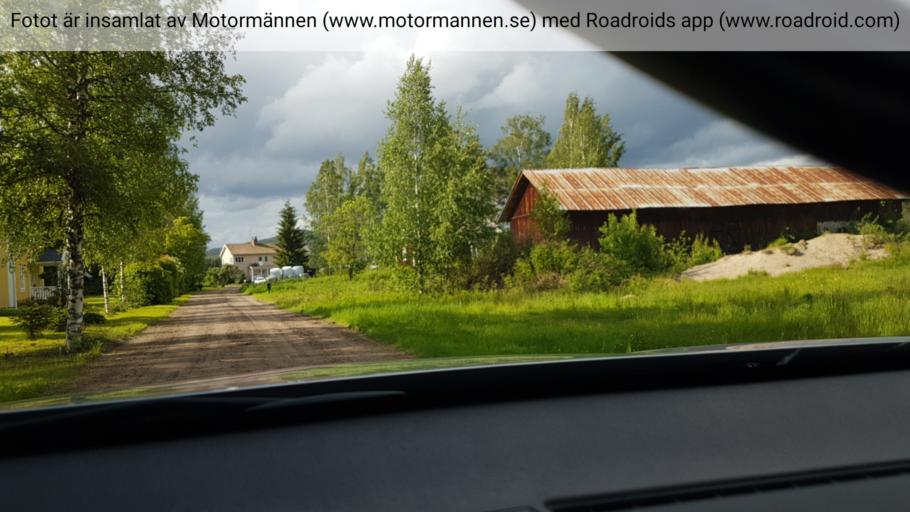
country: SE
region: Vaermland
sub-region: Torsby Kommun
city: Torsby
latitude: 60.6081
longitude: 13.0573
